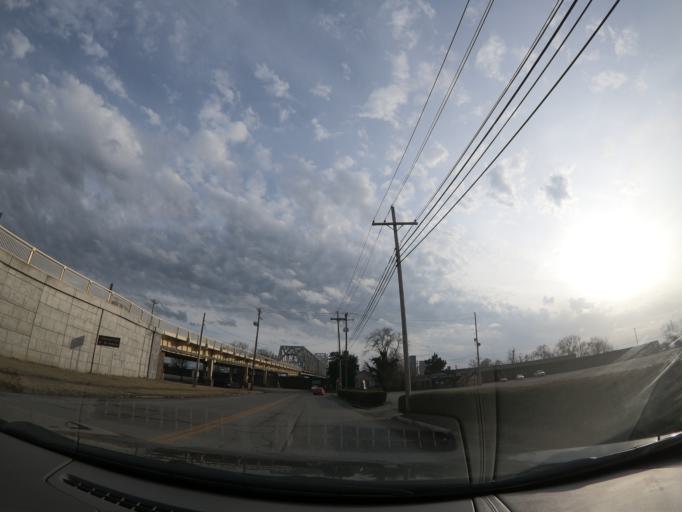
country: US
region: Indiana
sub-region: Clark County
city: Jeffersonville
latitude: 38.2701
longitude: -85.7505
